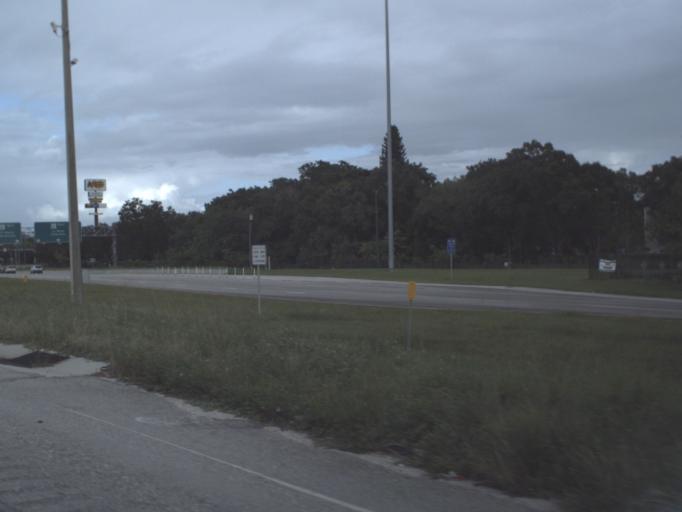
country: US
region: Florida
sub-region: Lee County
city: Tice
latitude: 26.6814
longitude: -81.7985
